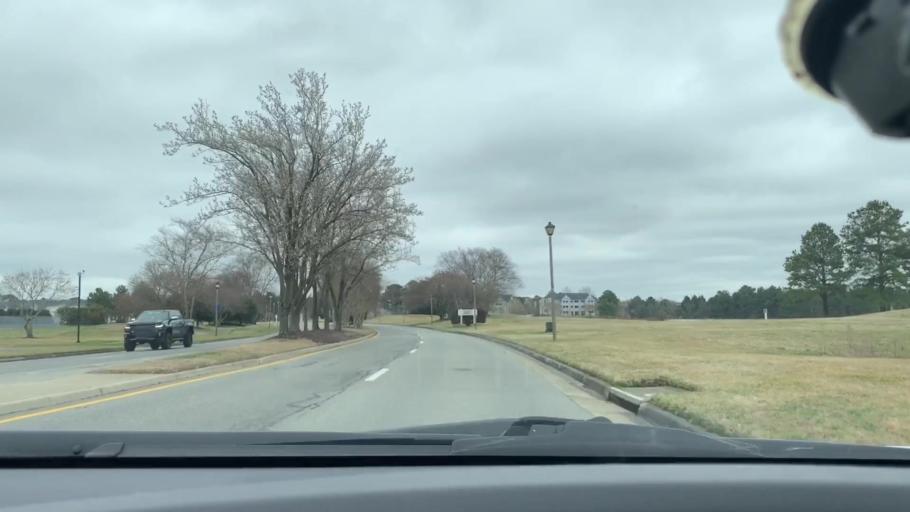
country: US
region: Virginia
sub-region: York County
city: Yorktown
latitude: 37.1195
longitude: -76.5019
